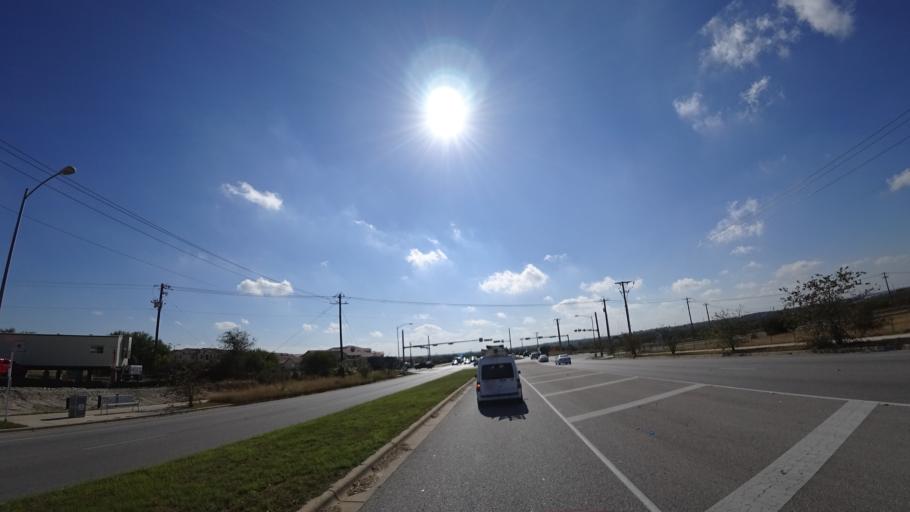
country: US
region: Texas
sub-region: Travis County
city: Windemere
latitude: 30.4334
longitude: -97.6533
